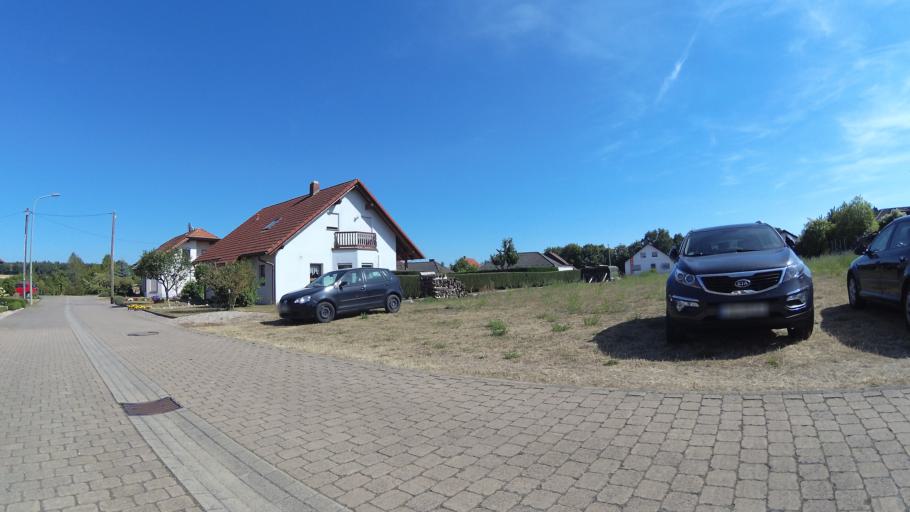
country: DE
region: Saarland
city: Gersheim
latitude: 49.1446
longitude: 7.2824
